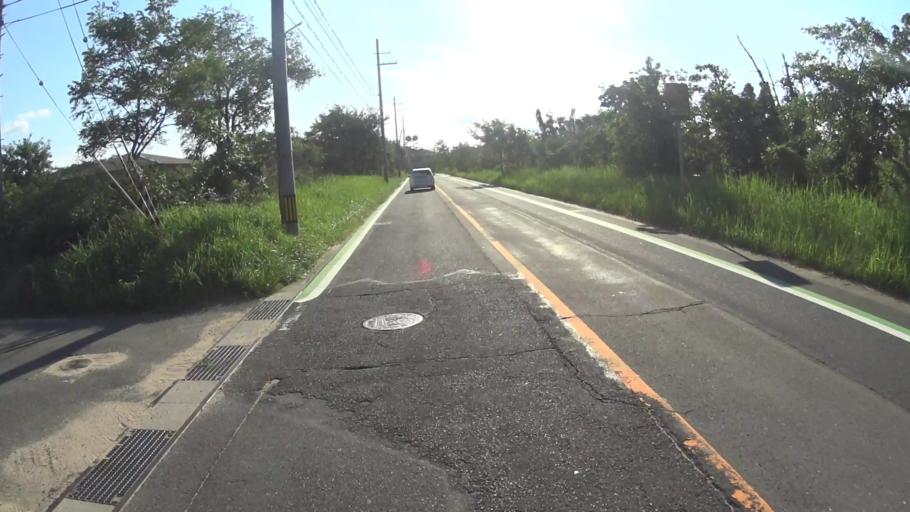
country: JP
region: Hyogo
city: Toyooka
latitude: 35.6581
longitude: 134.9620
